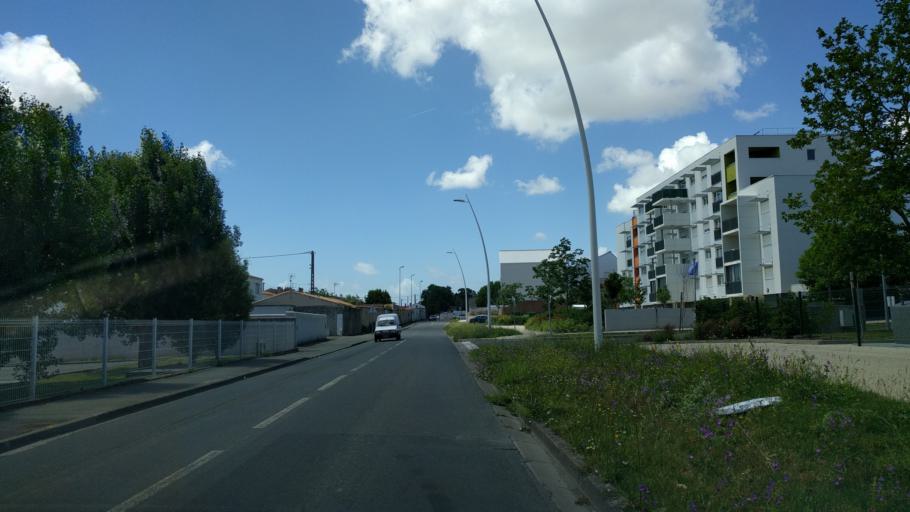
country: FR
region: Poitou-Charentes
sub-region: Departement de la Charente-Maritime
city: La Rochelle
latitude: 46.1639
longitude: -1.1268
